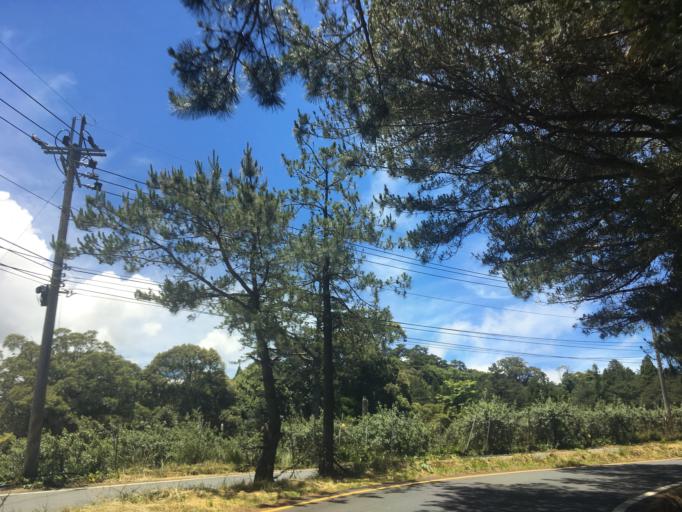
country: TW
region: Taiwan
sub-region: Nantou
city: Puli
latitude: 24.2349
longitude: 121.2439
